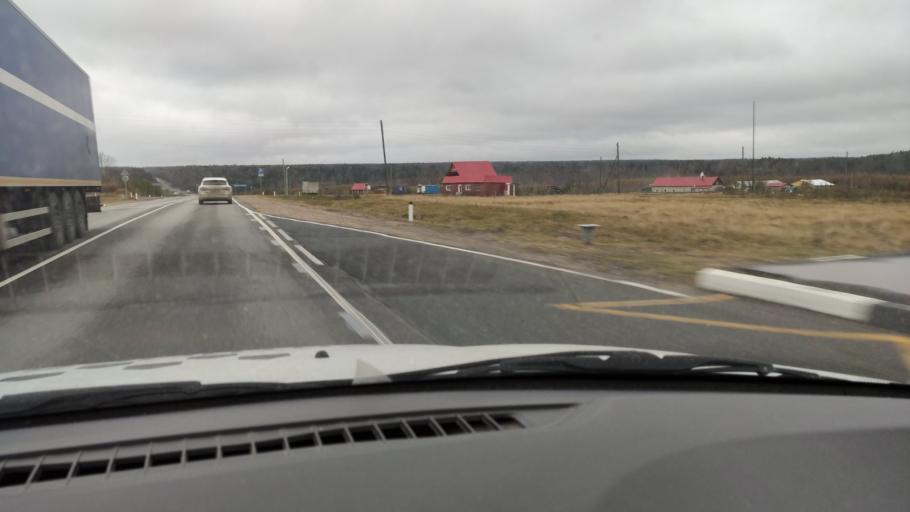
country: RU
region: Kirov
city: Chernaya Kholunitsa
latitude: 58.8585
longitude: 51.7076
